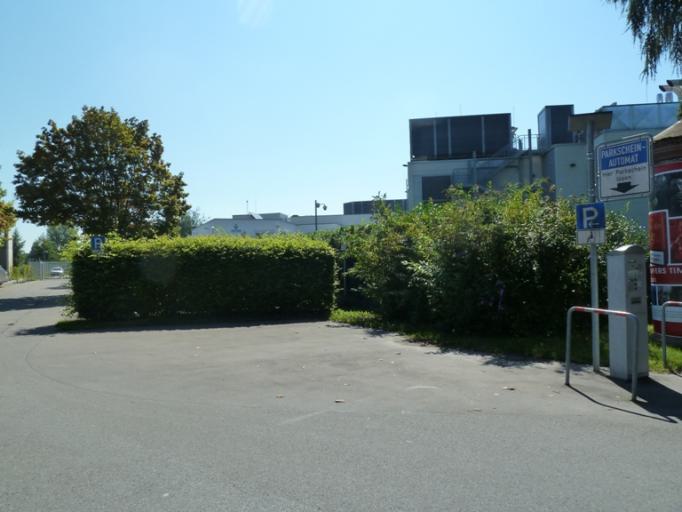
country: DE
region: Baden-Wuerttemberg
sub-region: Tuebingen Region
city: Langenargen
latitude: 47.5990
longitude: 9.5458
